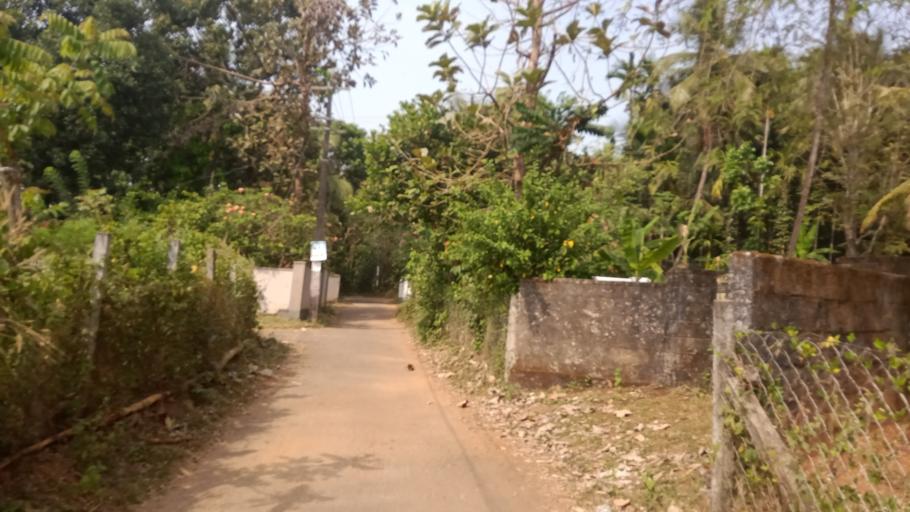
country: IN
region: Kerala
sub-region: Palakkad district
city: Cherpulassery
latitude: 10.8859
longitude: 76.3151
